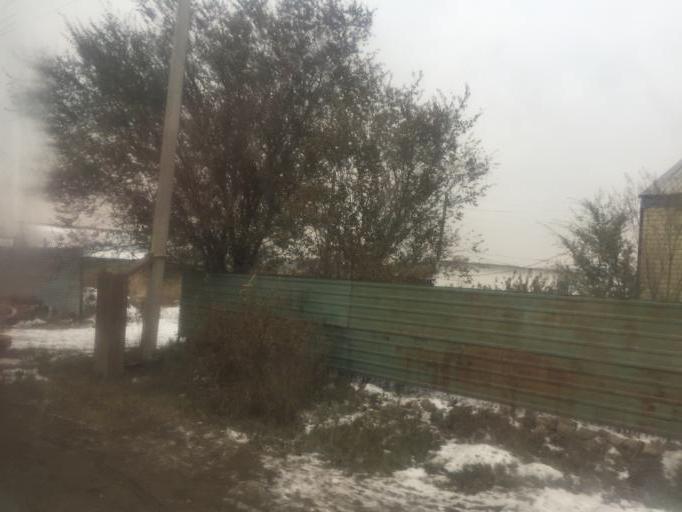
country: KZ
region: Astana Qalasy
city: Astana
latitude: 51.2016
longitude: 71.4106
